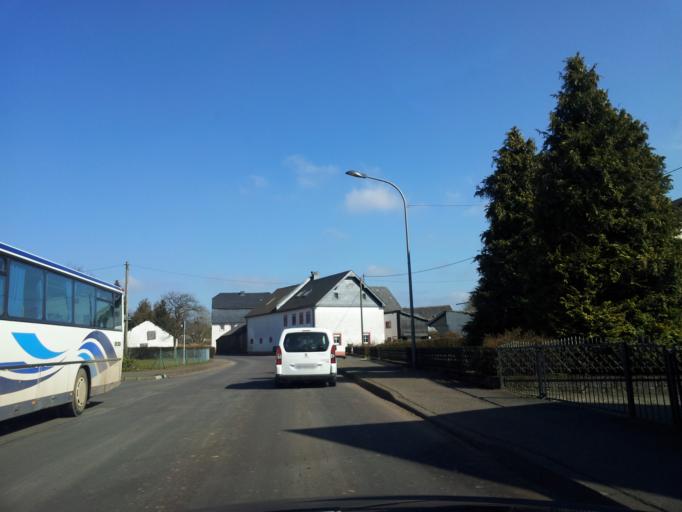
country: DE
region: Rheinland-Pfalz
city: Grosslangenfeld
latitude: 50.2208
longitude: 6.2531
